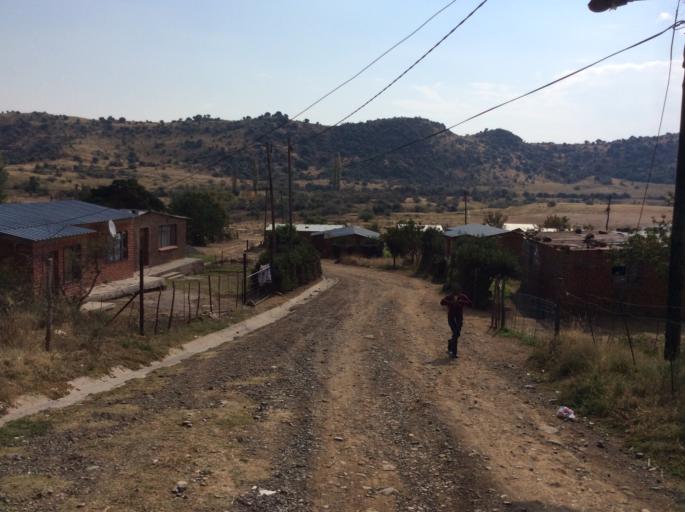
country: LS
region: Mafeteng
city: Mafeteng
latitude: -29.9818
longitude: 27.0065
